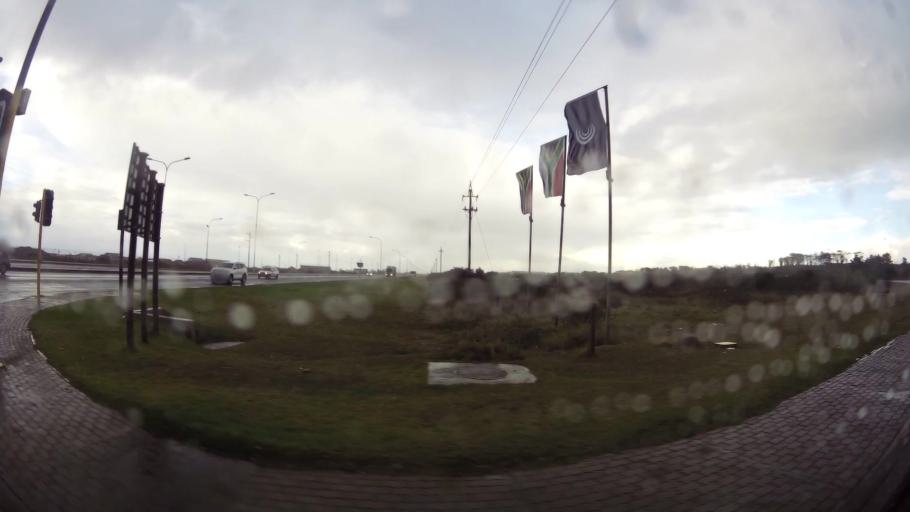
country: ZA
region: Western Cape
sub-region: Eden District Municipality
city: Mossel Bay
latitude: -34.1829
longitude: 22.0906
